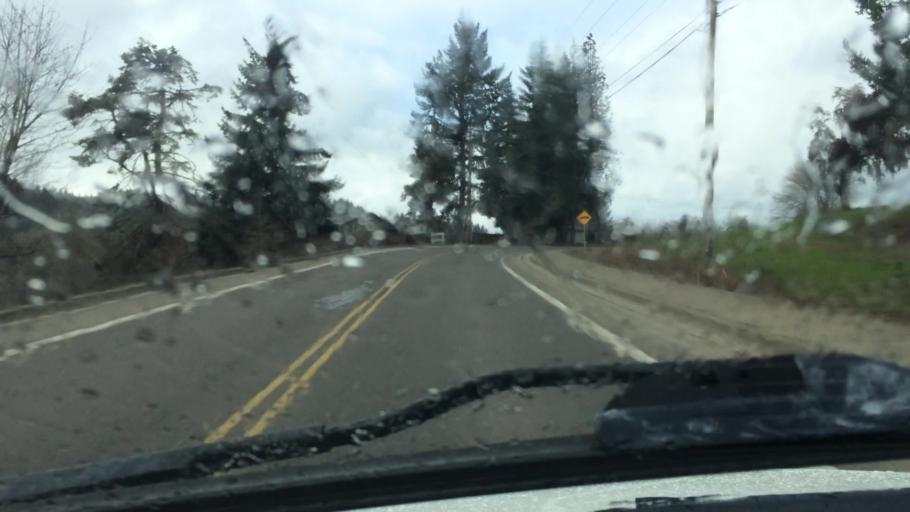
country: US
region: Oregon
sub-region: Polk County
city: Grand Ronde
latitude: 45.0648
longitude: -123.6110
